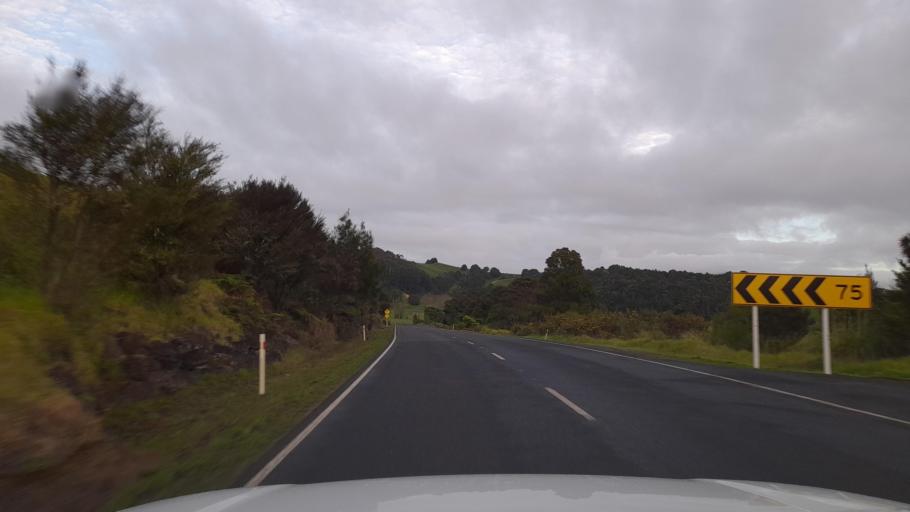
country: NZ
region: Northland
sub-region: Whangarei
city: Maungatapere
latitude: -35.7199
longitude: 174.0362
